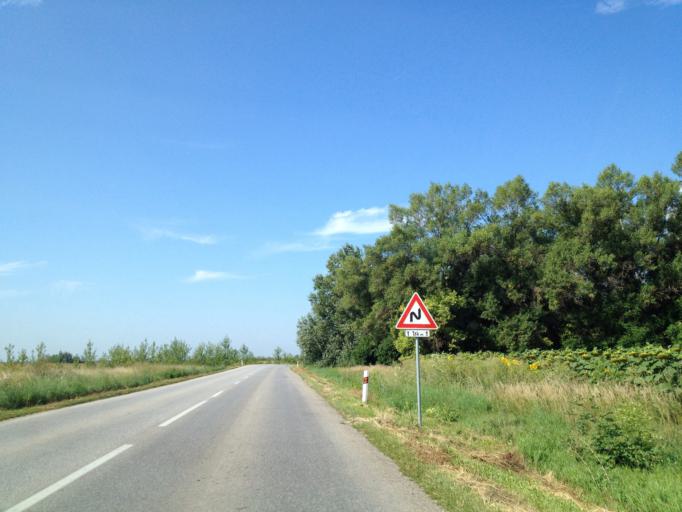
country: SK
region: Nitriansky
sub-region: Okres Komarno
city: Hurbanovo
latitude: 47.8079
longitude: 18.2023
